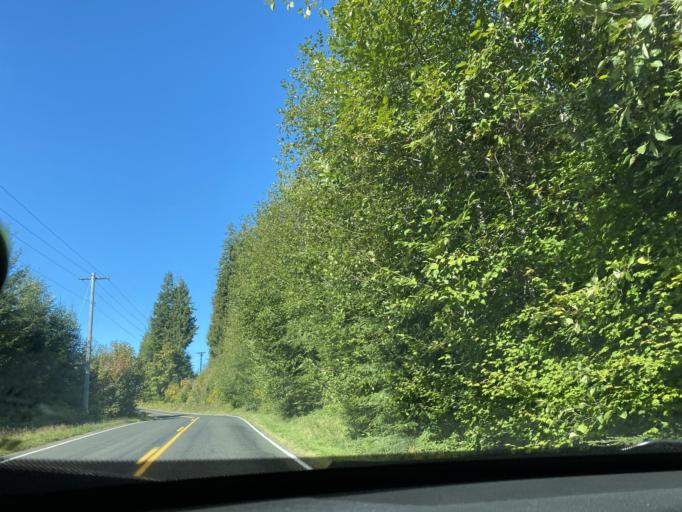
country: US
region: Washington
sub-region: Clallam County
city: Forks
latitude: 47.9485
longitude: -124.5051
